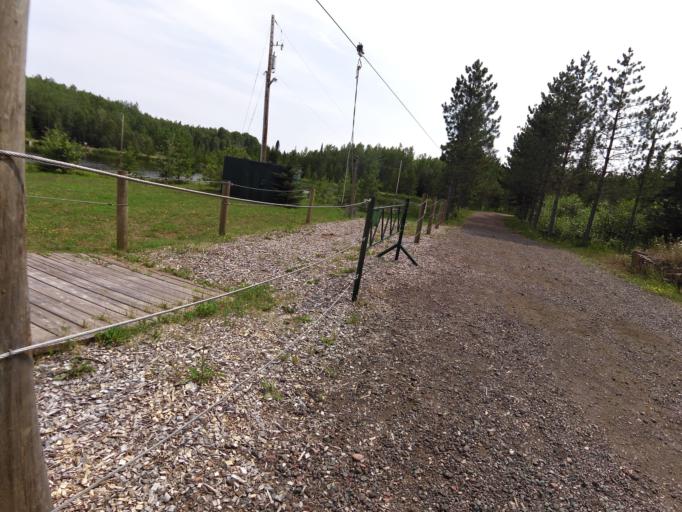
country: CA
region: Ontario
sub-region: Thunder Bay District
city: Thunder Bay
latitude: 48.7963
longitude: -88.6195
